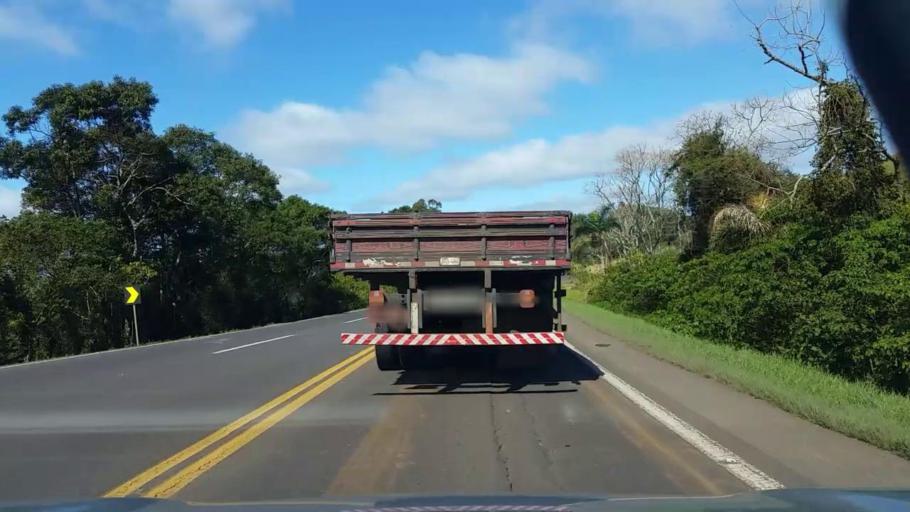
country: BR
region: Rio Grande do Sul
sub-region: Encantado
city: Encantado
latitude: -29.1641
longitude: -52.2208
